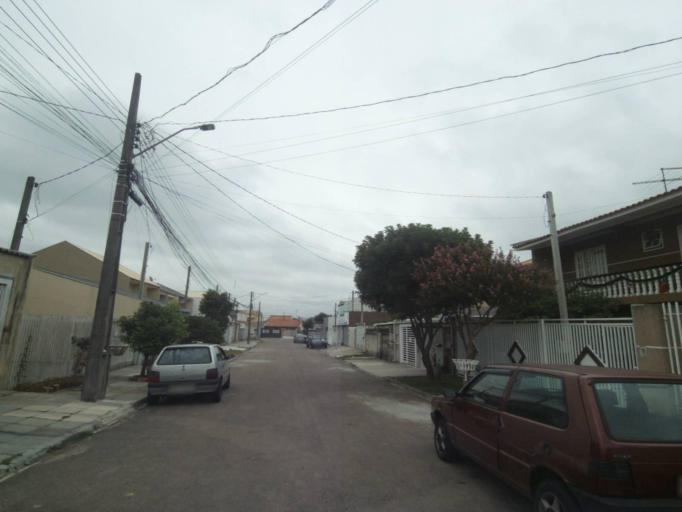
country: BR
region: Parana
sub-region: Araucaria
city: Araucaria
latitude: -25.5396
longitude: -49.3361
